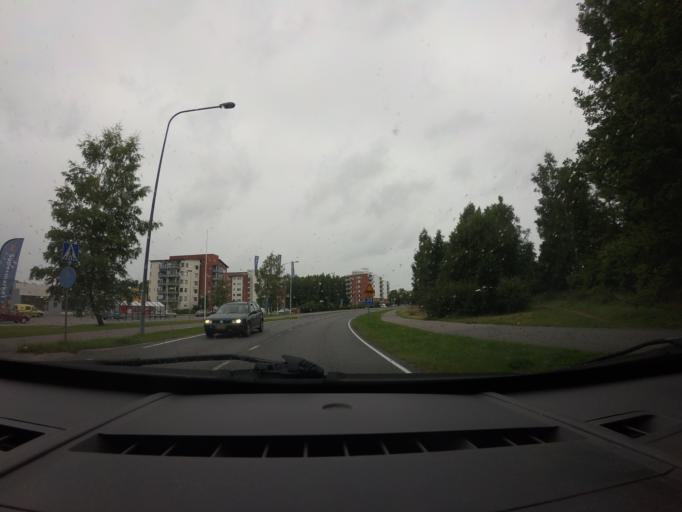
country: FI
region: Varsinais-Suomi
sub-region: Turku
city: Turku
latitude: 60.4176
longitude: 22.3024
